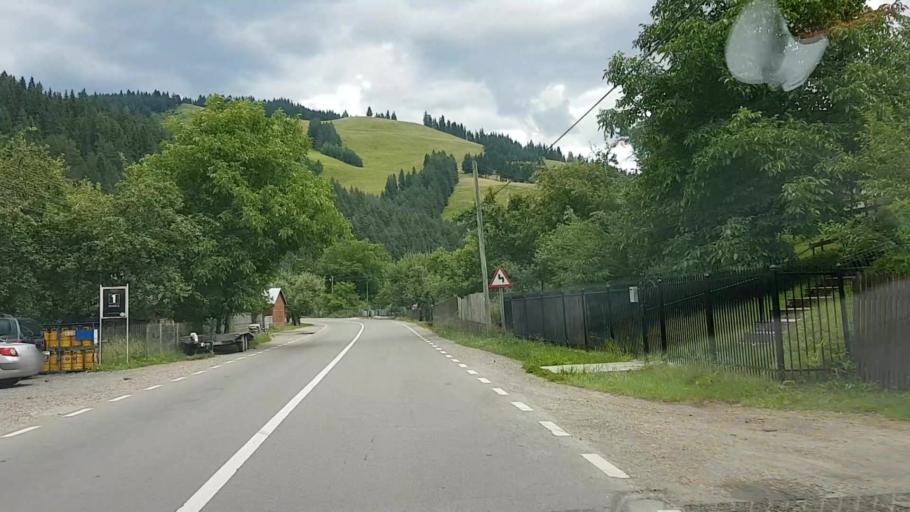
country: RO
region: Neamt
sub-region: Comuna Farcasa
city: Farcasa
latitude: 47.1353
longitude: 25.8924
